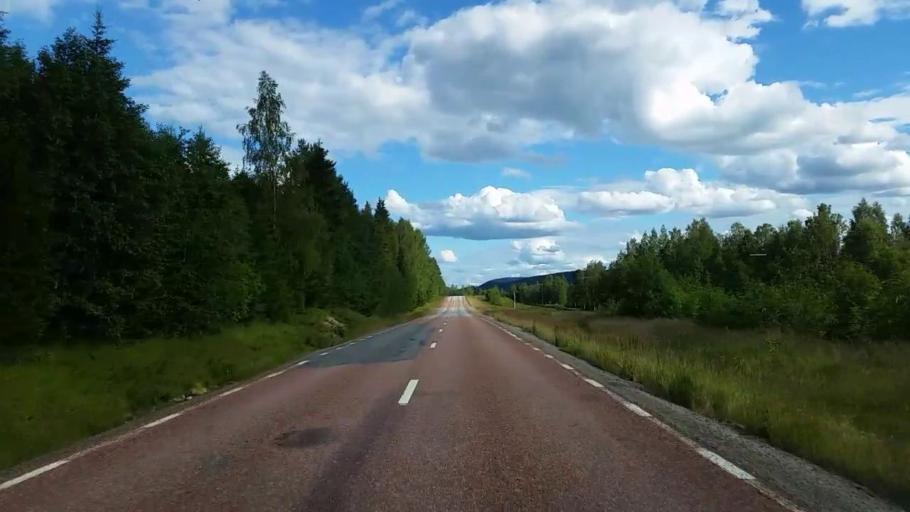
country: SE
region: Gaevleborg
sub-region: Ljusdals Kommun
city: Farila
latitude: 62.1369
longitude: 15.6912
